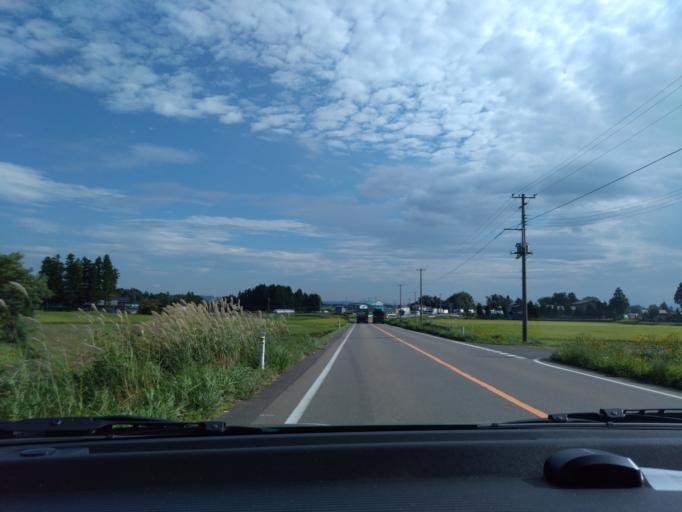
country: JP
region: Iwate
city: Hanamaki
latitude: 39.4645
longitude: 141.1015
